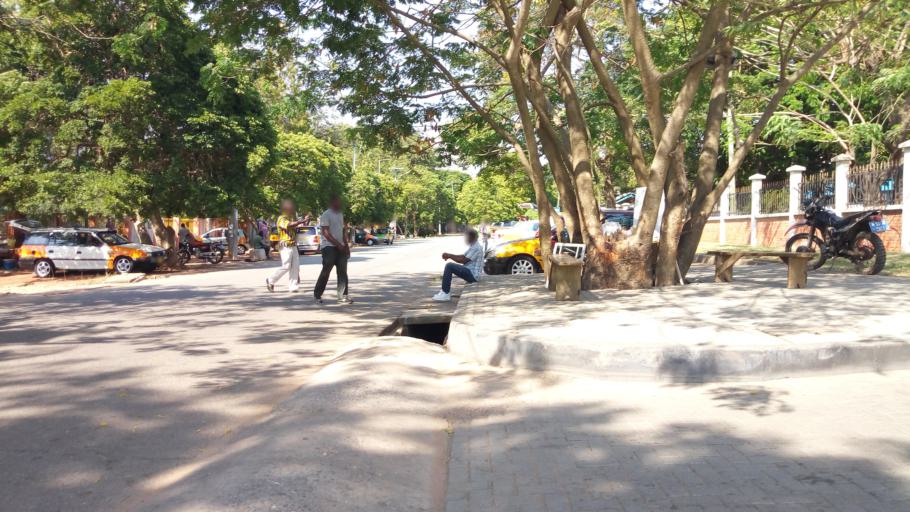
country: GH
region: Greater Accra
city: Accra
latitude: 5.5550
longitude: -0.1983
